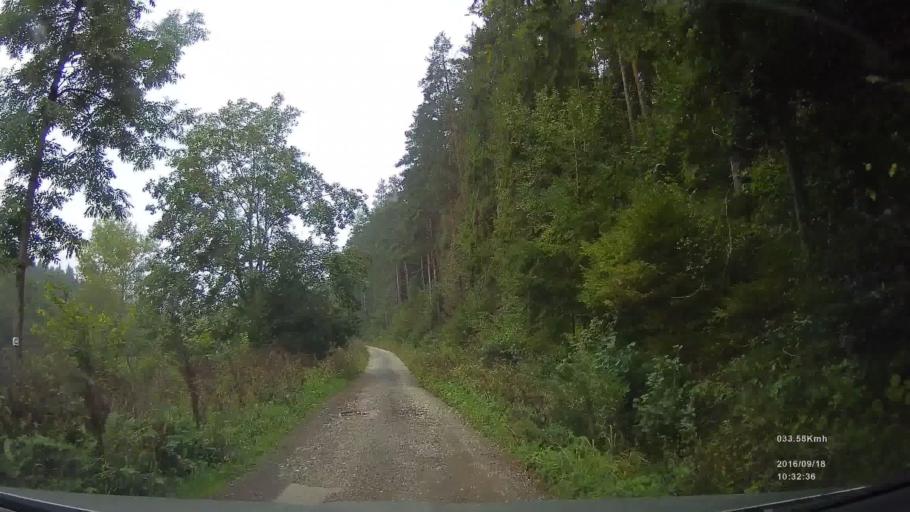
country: SK
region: Presovsky
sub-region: Okres Presov
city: Levoca
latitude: 48.9664
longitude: 20.6211
